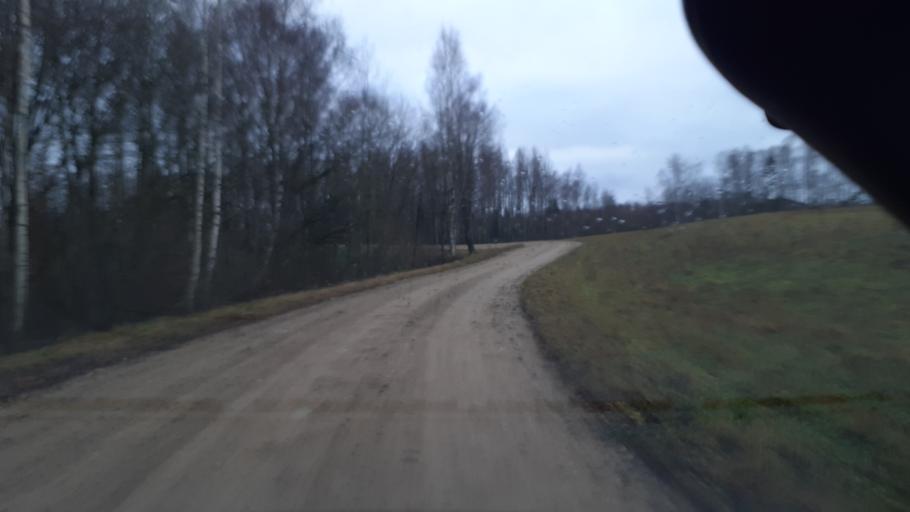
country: LV
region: Alsunga
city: Alsunga
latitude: 56.8918
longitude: 21.6915
